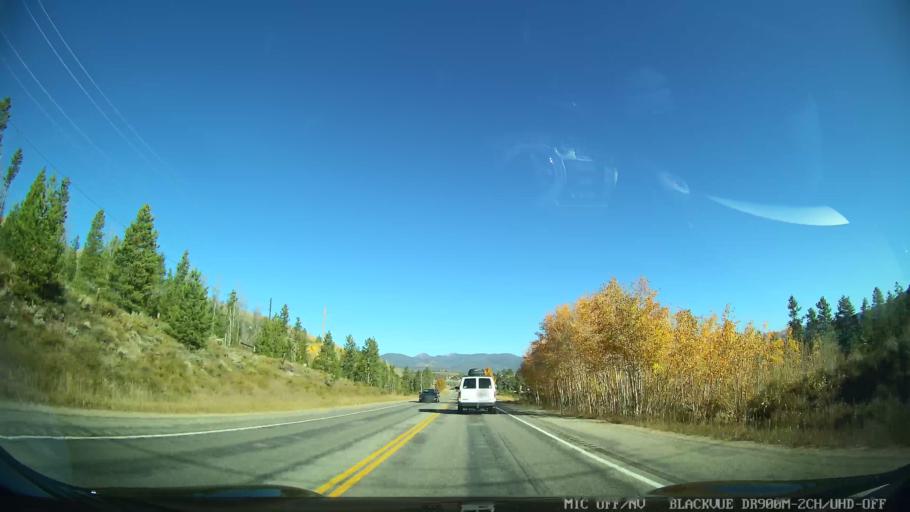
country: US
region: Colorado
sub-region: Grand County
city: Granby
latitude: 40.1537
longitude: -105.8892
